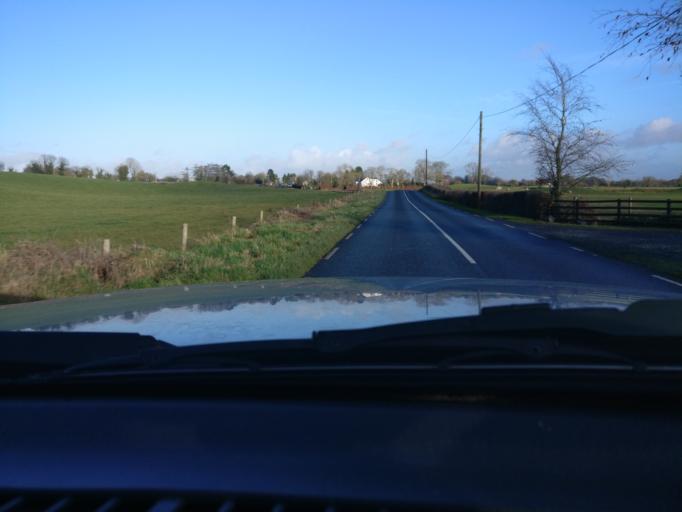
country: IE
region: Leinster
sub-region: An Iarmhi
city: An Muileann gCearr
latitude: 53.4913
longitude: -7.4369
